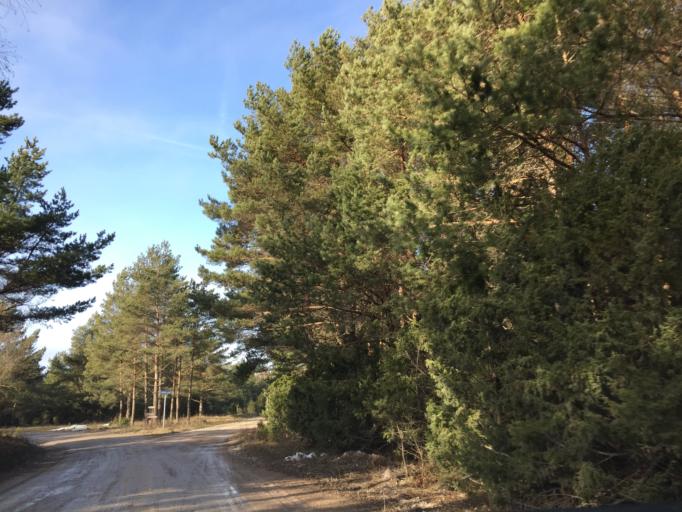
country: EE
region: Saare
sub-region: Kuressaare linn
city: Kuressaare
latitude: 58.4702
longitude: 21.9749
